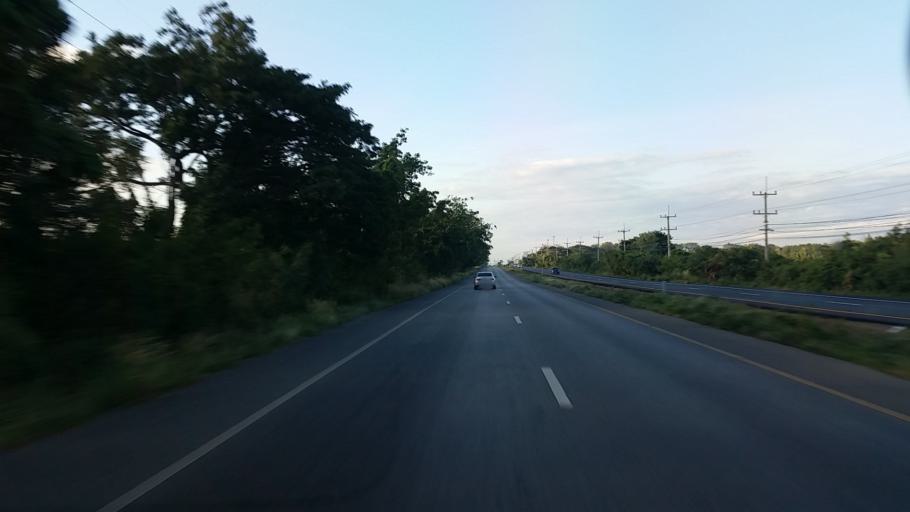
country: TH
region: Lop Buri
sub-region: Amphoe Tha Luang
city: Tha Luang
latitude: 15.1006
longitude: 101.0197
